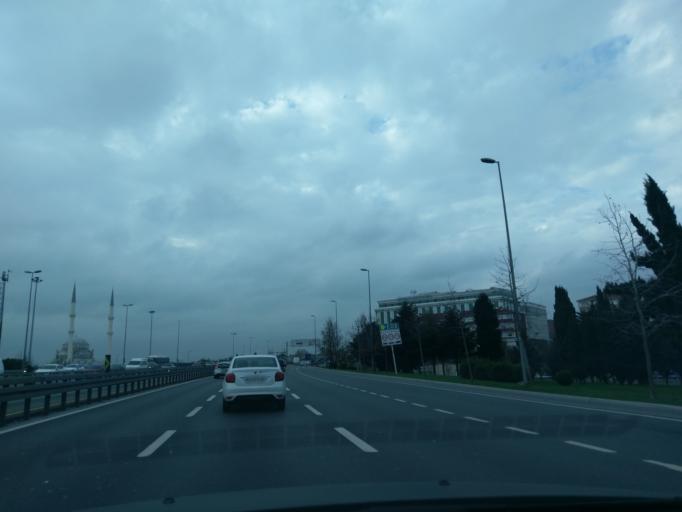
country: TR
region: Istanbul
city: Bahcelievler
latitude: 40.9905
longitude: 28.7933
